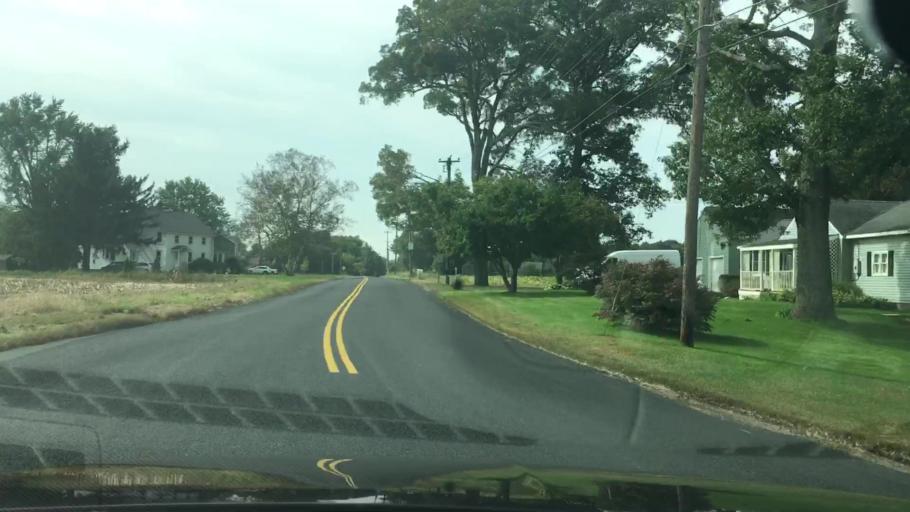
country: US
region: Connecticut
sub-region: Hartford County
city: Broad Brook
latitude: 41.8945
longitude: -72.5274
